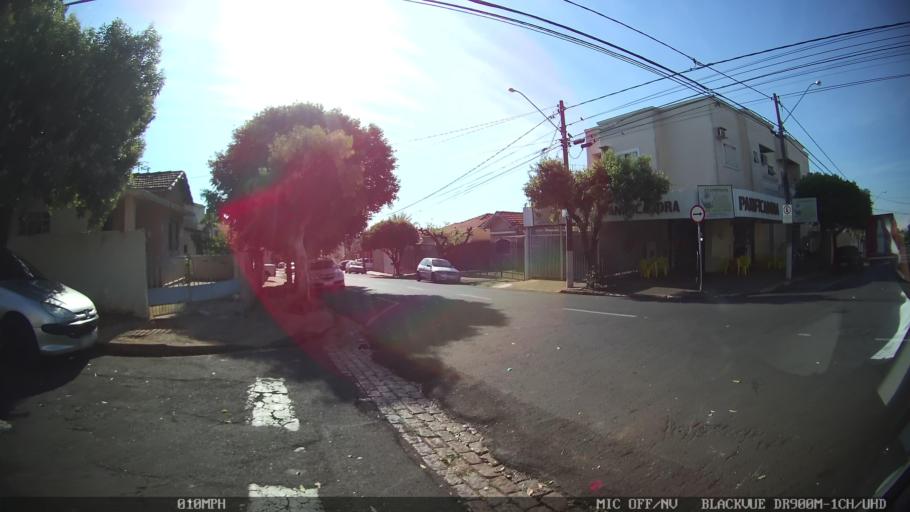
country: BR
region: Sao Paulo
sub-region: Sao Jose Do Rio Preto
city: Sao Jose do Rio Preto
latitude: -20.7998
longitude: -49.3930
